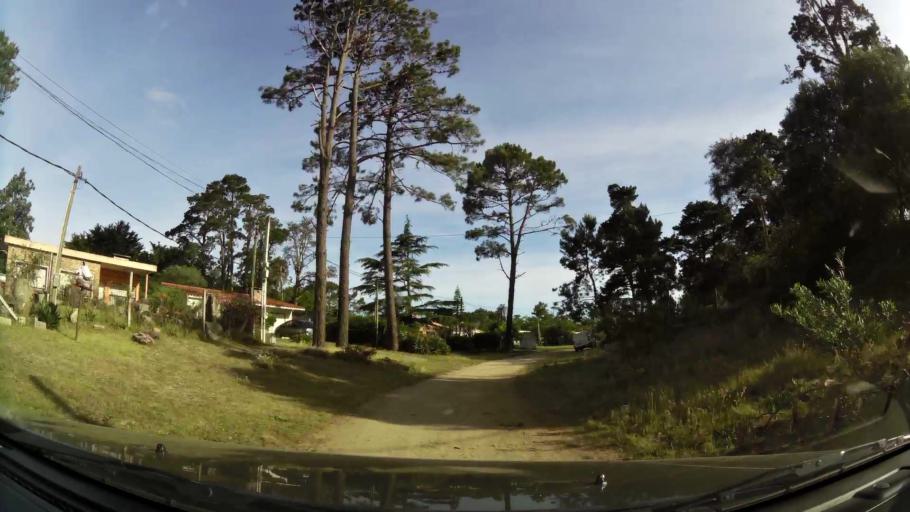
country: UY
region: Canelones
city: Empalme Olmos
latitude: -34.7811
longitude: -55.8541
